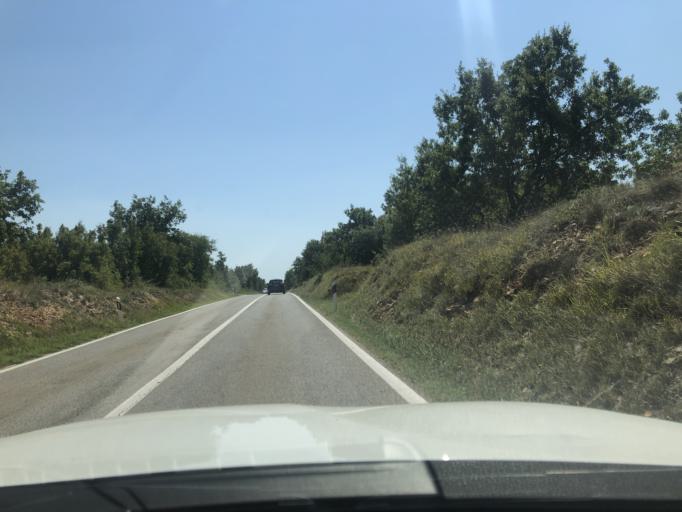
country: HR
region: Istarska
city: Vodnjan
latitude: 45.0134
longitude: 13.8076
